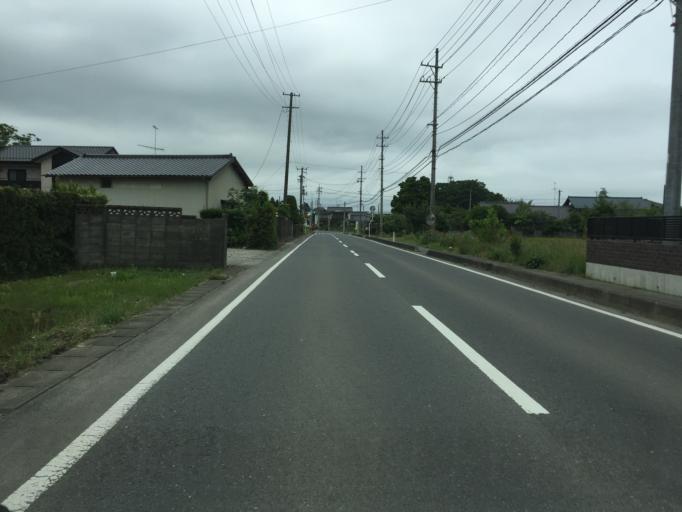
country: JP
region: Miyagi
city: Marumori
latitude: 37.7739
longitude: 140.9127
